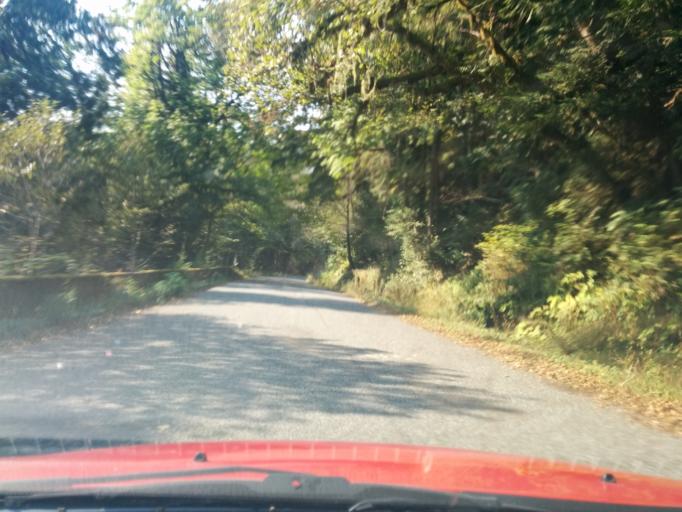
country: US
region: Washington
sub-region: Snohomish County
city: Darrington
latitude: 48.5228
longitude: -121.3768
